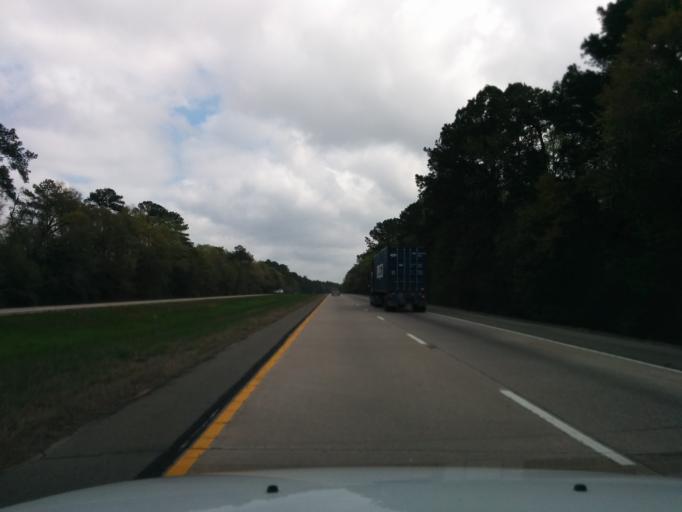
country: US
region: Georgia
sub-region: Bryan County
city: Pembroke
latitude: 32.2133
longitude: -81.5122
